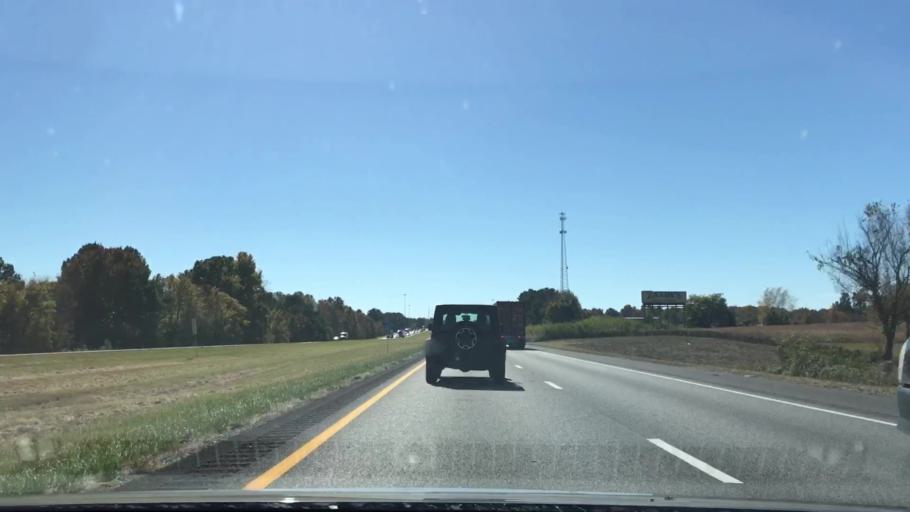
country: US
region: Tennessee
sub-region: Sumner County
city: White House
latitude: 36.4782
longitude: -86.6783
